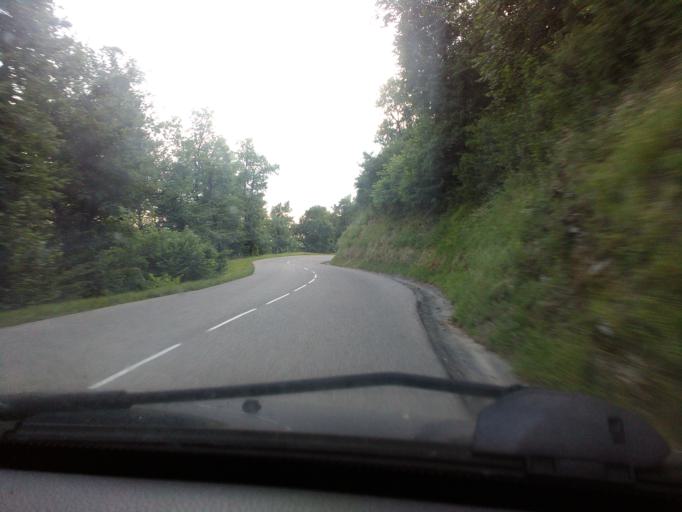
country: FR
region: Rhone-Alpes
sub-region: Departement de l'Isere
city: Saint-Egreve
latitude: 45.2474
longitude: 5.6951
